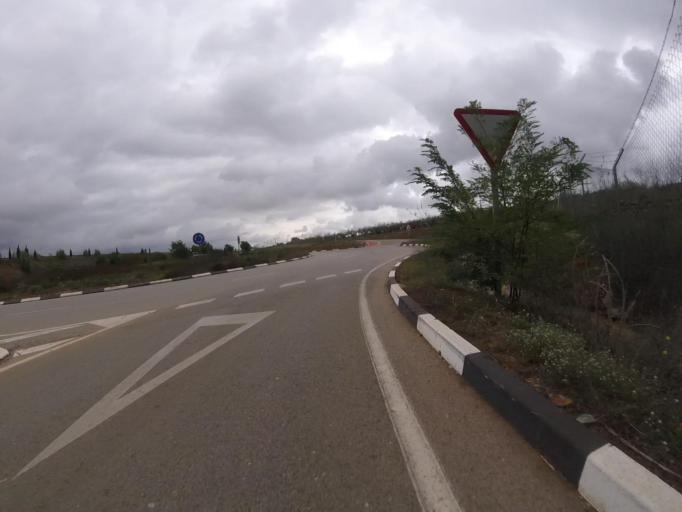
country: ES
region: Valencia
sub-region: Provincia de Castello
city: Cabanes
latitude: 40.1663
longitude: 0.0419
